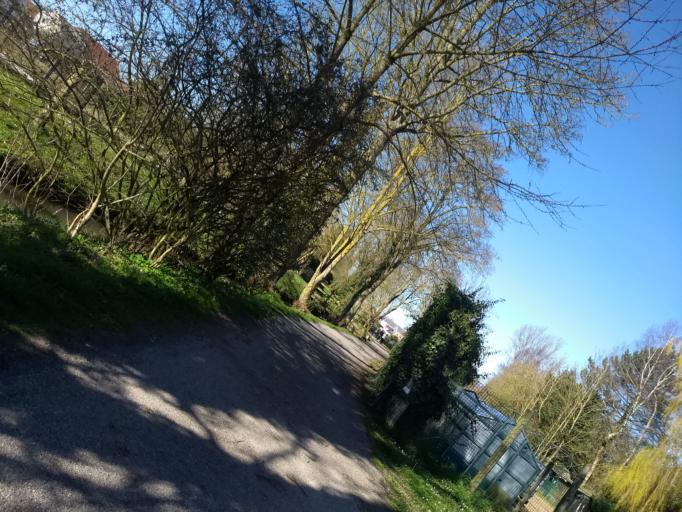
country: FR
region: Nord-Pas-de-Calais
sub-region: Departement du Pas-de-Calais
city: Achicourt
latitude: 50.2687
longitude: 2.7566
